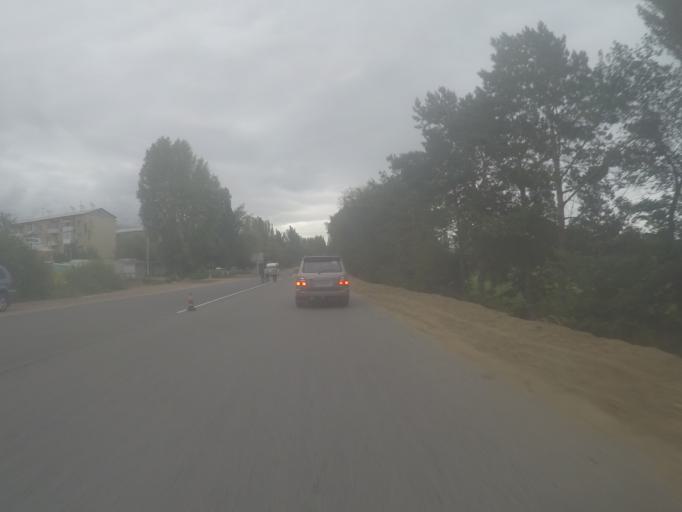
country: KG
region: Ysyk-Koel
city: Cholpon-Ata
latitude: 42.6744
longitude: 77.2988
